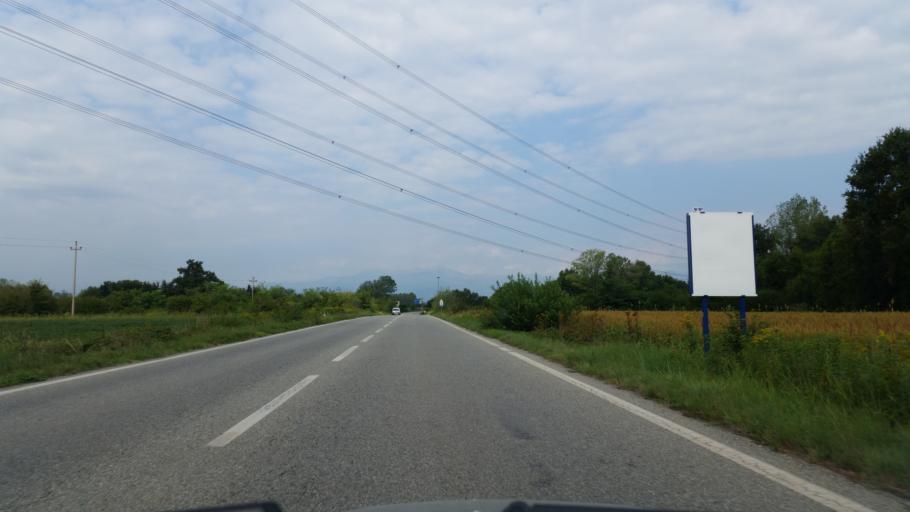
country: IT
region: Piedmont
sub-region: Provincia di Torino
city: Orio Canavese
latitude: 45.3087
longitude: 7.8558
